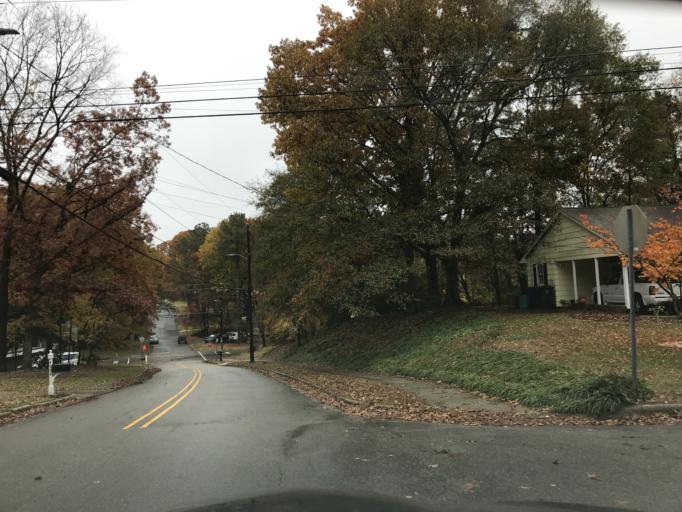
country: US
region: North Carolina
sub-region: Wake County
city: West Raleigh
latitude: 35.8375
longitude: -78.6219
